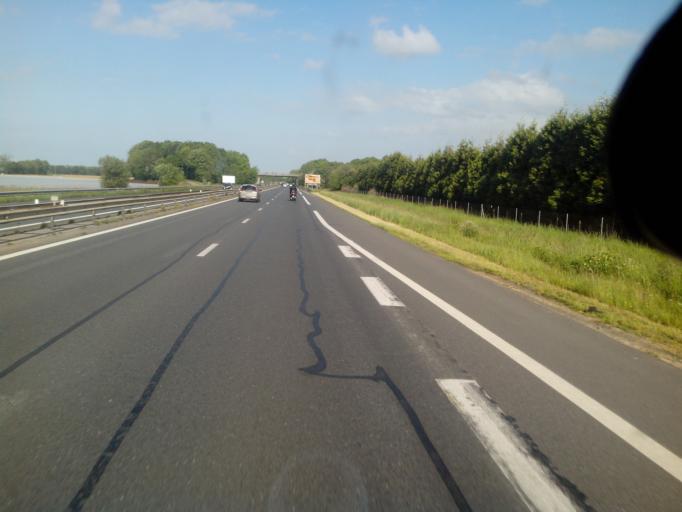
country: FR
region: Lower Normandy
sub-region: Departement du Calvados
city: Sannerville
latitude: 49.1681
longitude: -0.2368
